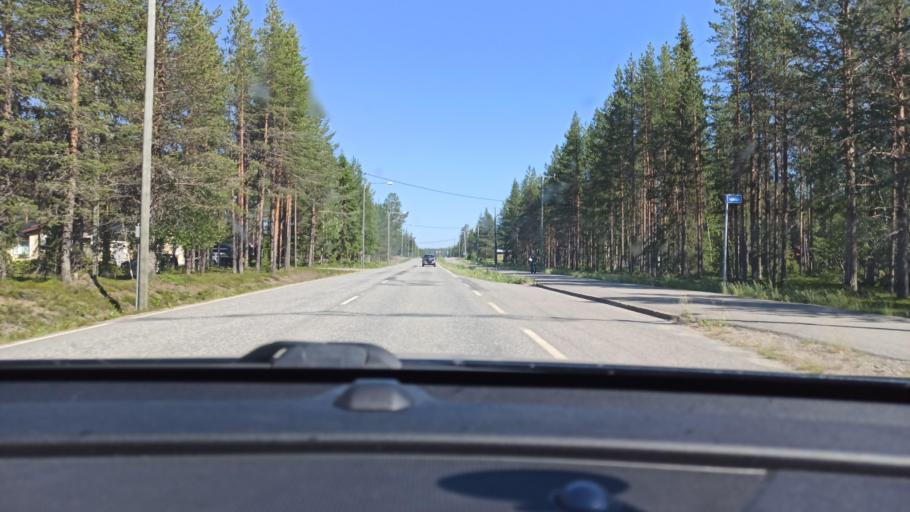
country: FI
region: Lapland
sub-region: Tunturi-Lappi
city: Kolari
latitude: 67.6209
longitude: 24.1540
